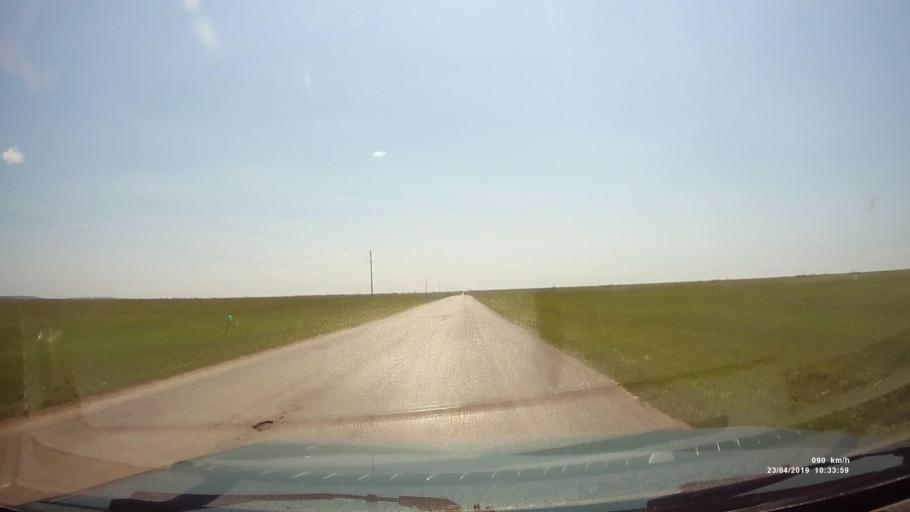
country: RU
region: Kalmykiya
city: Yashalta
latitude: 46.5684
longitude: 42.6043
